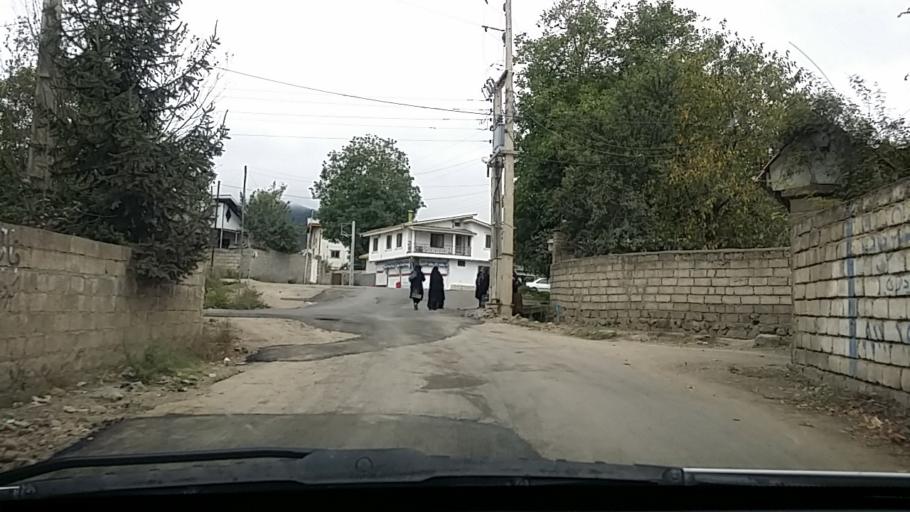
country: IR
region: Mazandaran
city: `Abbasabad
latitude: 36.5117
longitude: 51.1631
